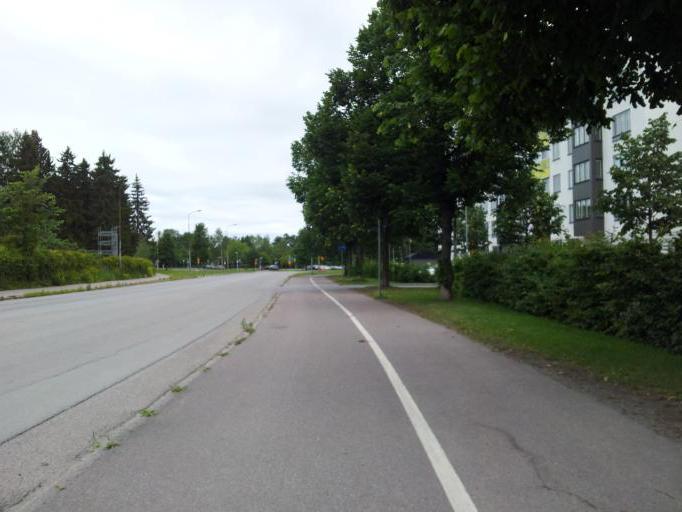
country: SE
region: Uppsala
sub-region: Uppsala Kommun
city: Uppsala
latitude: 59.8678
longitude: 17.6224
